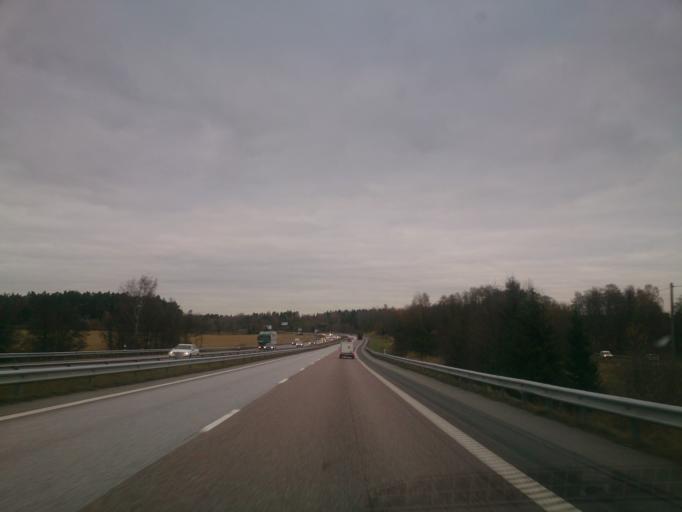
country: SE
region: Stockholm
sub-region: Sodertalje Kommun
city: Pershagen
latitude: 59.1398
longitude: 17.6479
